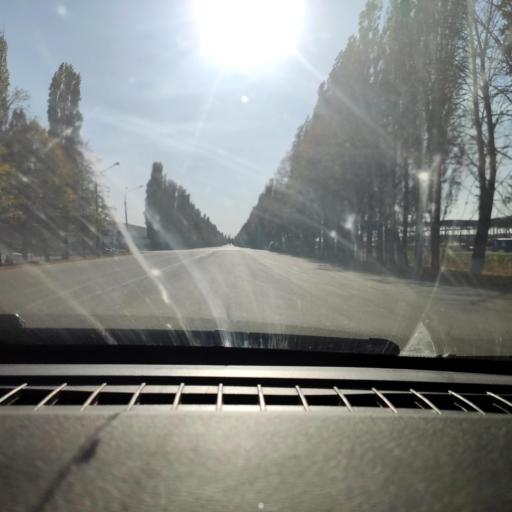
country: RU
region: Voronezj
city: Podgornoye
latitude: 51.8085
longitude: 39.2196
